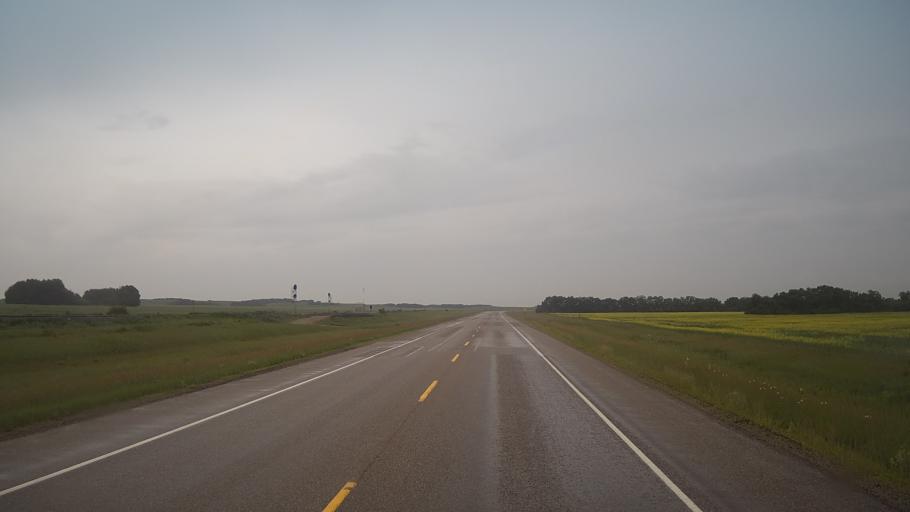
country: CA
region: Saskatchewan
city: Wilkie
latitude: 52.2359
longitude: -108.5534
